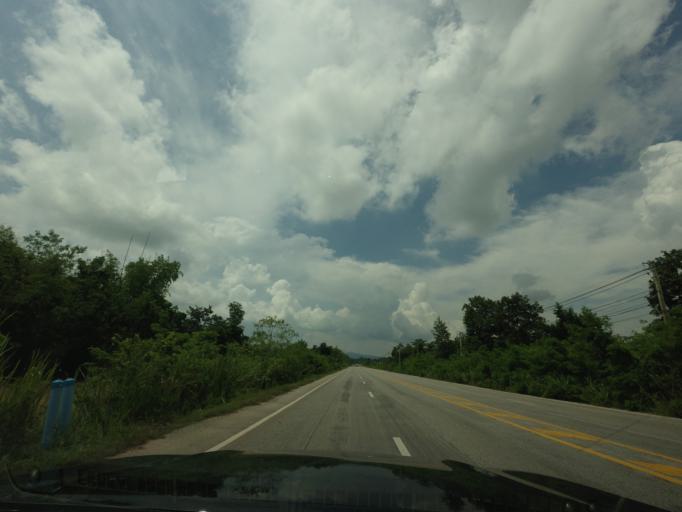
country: TH
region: Khon Kaen
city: Phu Wiang
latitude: 16.6773
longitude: 102.3340
